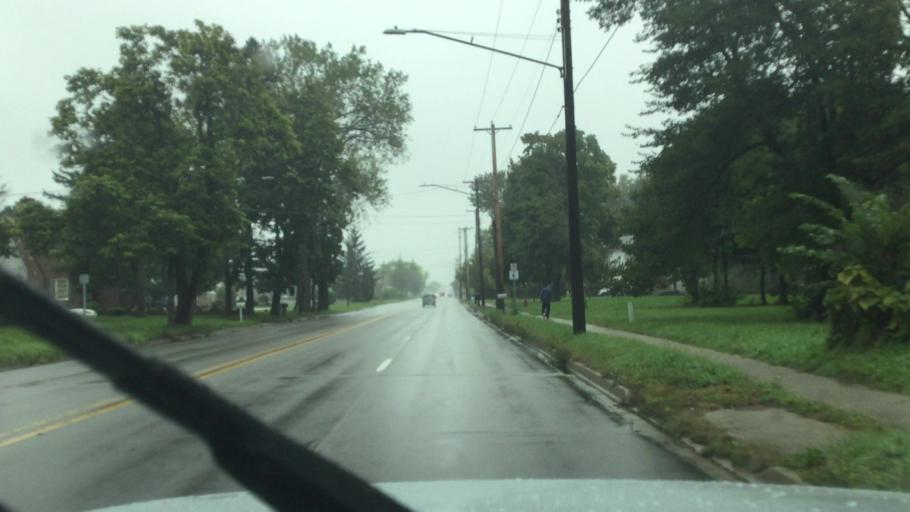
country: US
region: Michigan
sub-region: Saginaw County
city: Buena Vista
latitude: 43.4030
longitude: -83.9137
